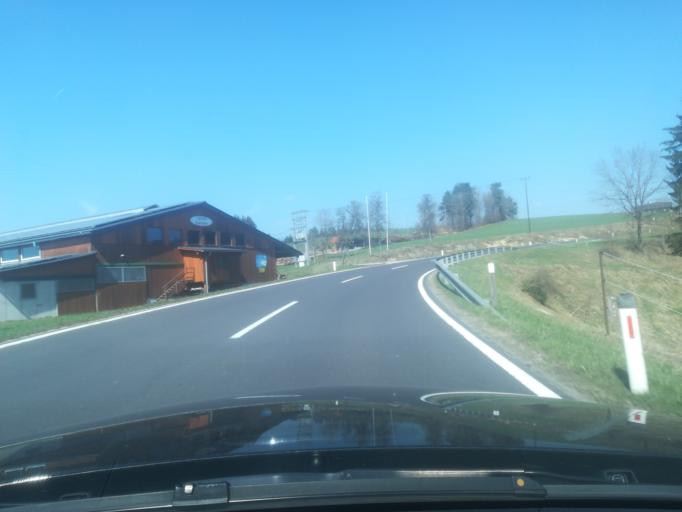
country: AT
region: Upper Austria
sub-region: Politischer Bezirk Perg
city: Perg
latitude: 48.3623
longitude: 14.6807
